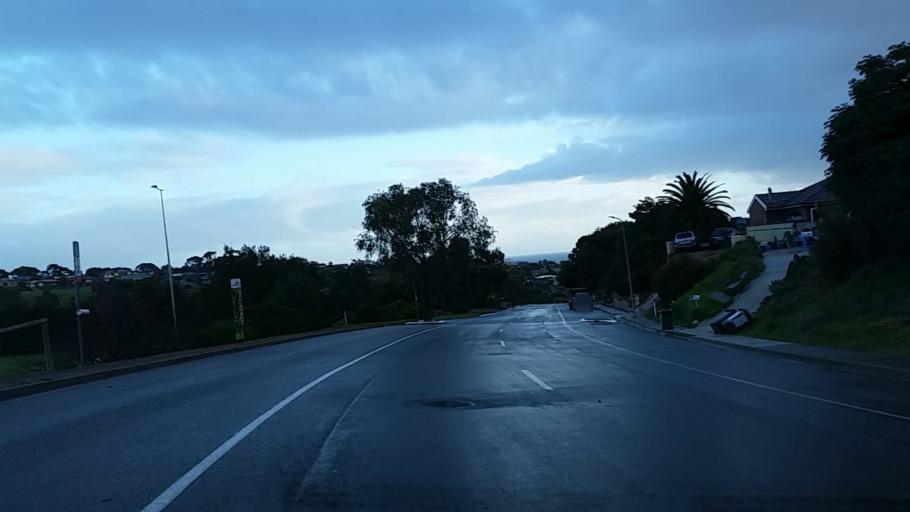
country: AU
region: South Australia
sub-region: Marion
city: Marino
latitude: -35.0692
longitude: 138.5113
